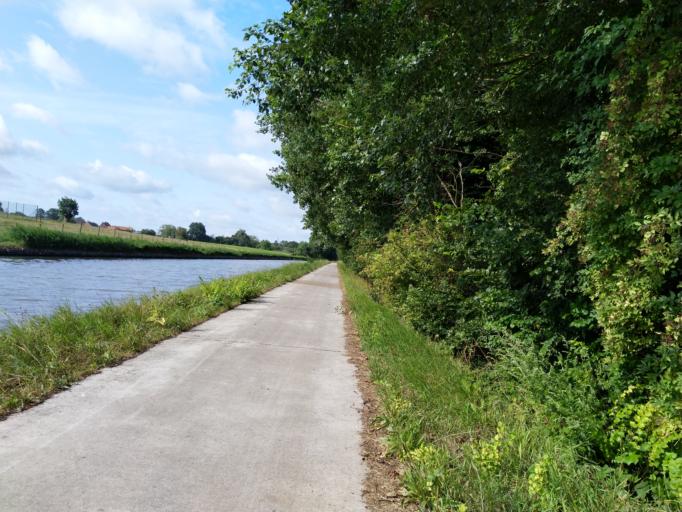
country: BE
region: Wallonia
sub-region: Province du Hainaut
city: Chievres
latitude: 50.5796
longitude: 3.7751
